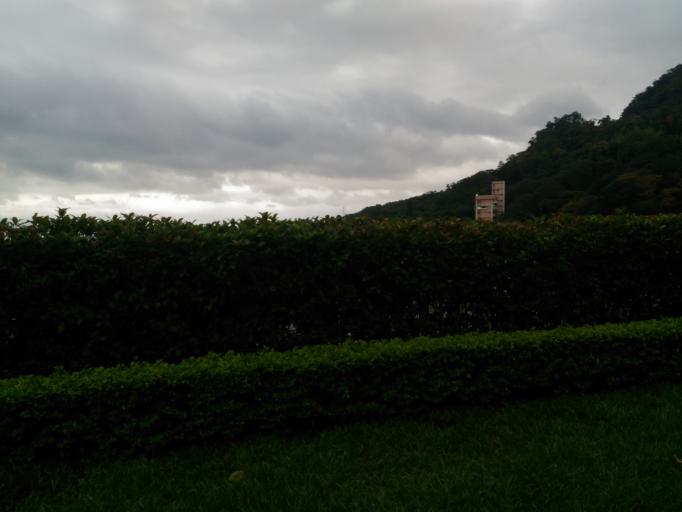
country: TW
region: Taipei
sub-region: Taipei
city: Banqiao
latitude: 24.9515
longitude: 121.4459
